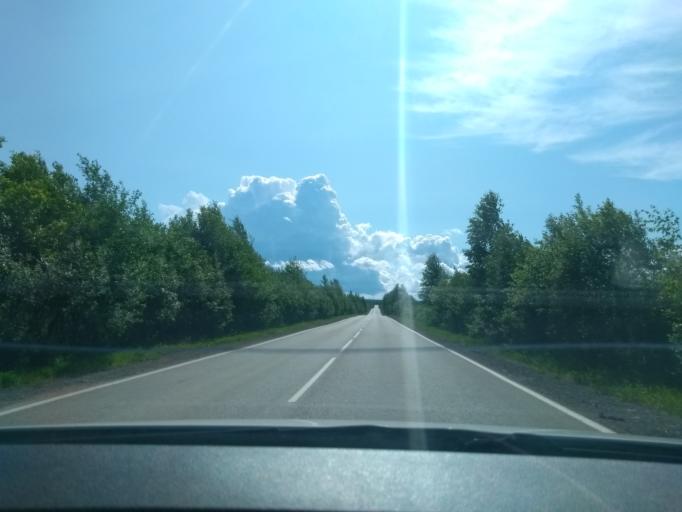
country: RU
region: Perm
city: Bershet'
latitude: 57.8203
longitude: 56.4345
